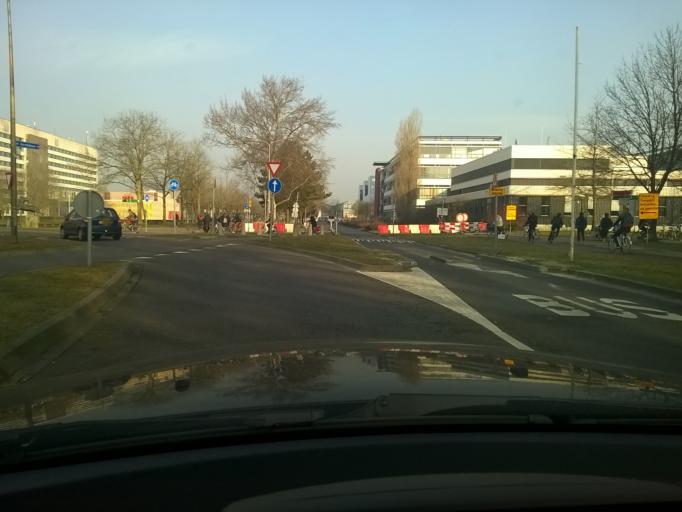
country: NL
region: Groningen
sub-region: Gemeente Groningen
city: Korrewegwijk
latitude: 53.2379
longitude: 6.5375
